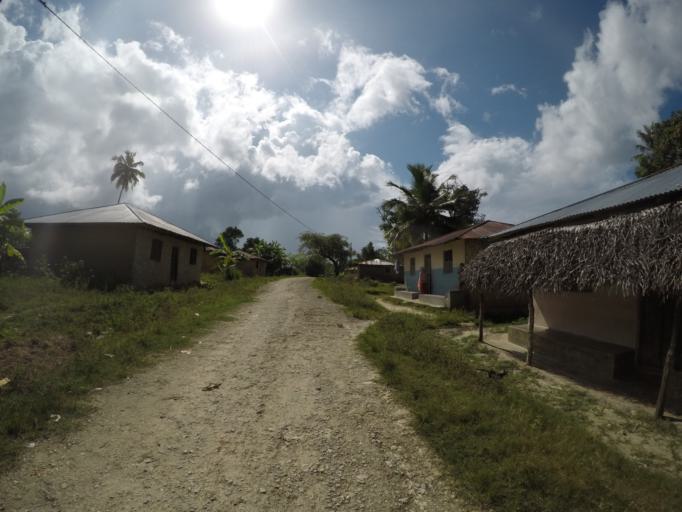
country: TZ
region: Pemba South
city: Mtambile
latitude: -5.3487
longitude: 39.6960
